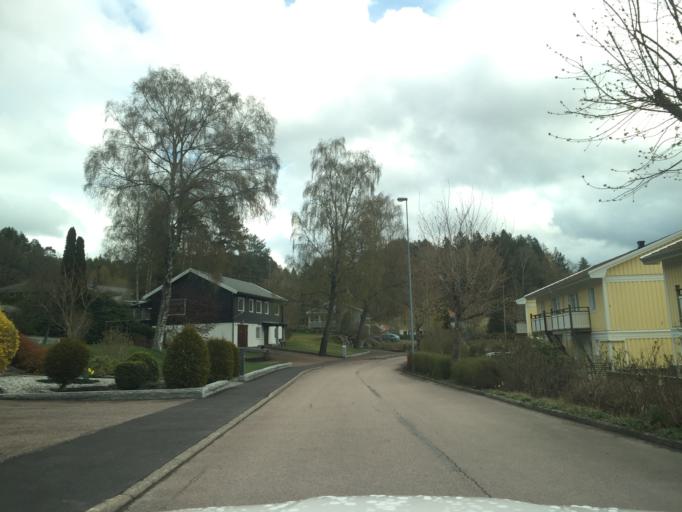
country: SE
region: Vaestra Goetaland
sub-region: Kungalvs Kommun
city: Kungalv
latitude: 57.8903
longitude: 11.9606
